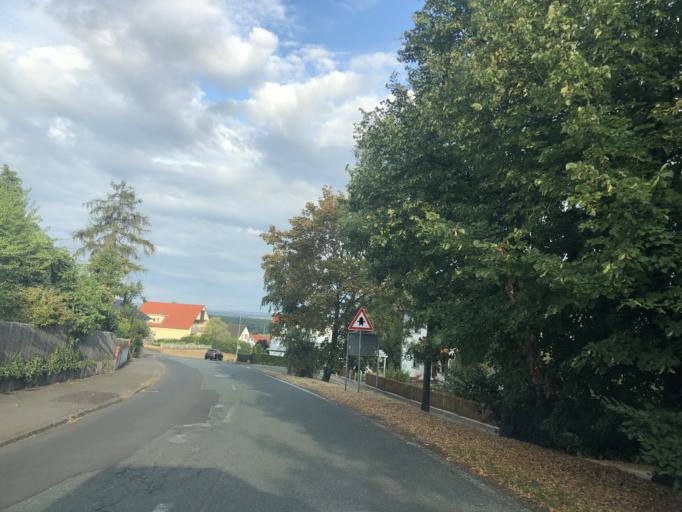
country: DE
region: Hesse
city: Amoneburg
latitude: 50.7951
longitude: 8.9253
